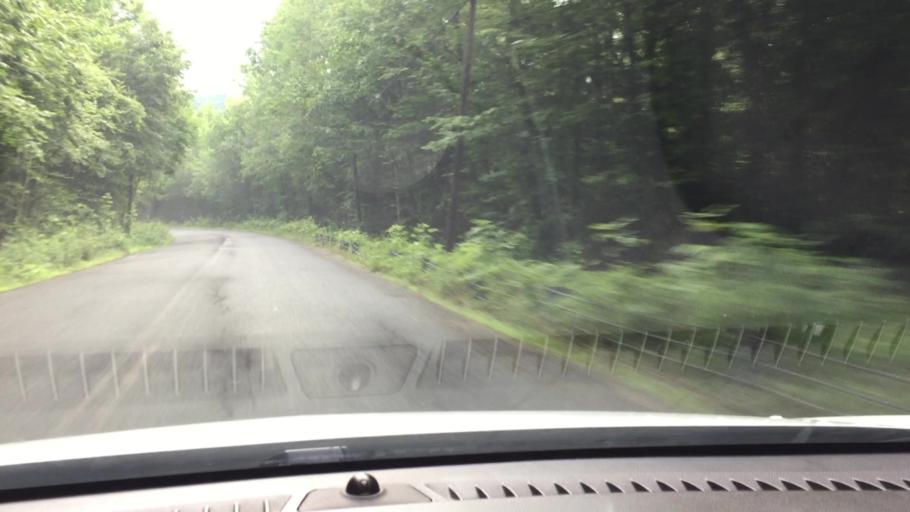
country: US
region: Massachusetts
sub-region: Hampshire County
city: Chesterfield
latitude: 42.2931
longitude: -72.9054
